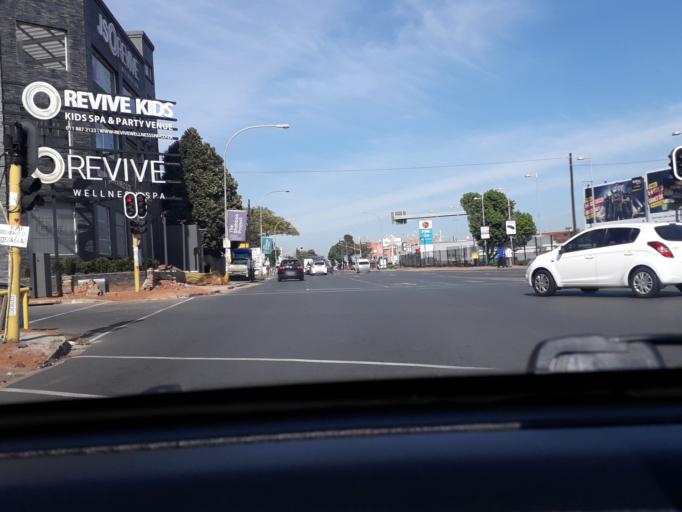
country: ZA
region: Gauteng
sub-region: City of Johannesburg Metropolitan Municipality
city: Johannesburg
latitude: -26.1388
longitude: 28.0899
